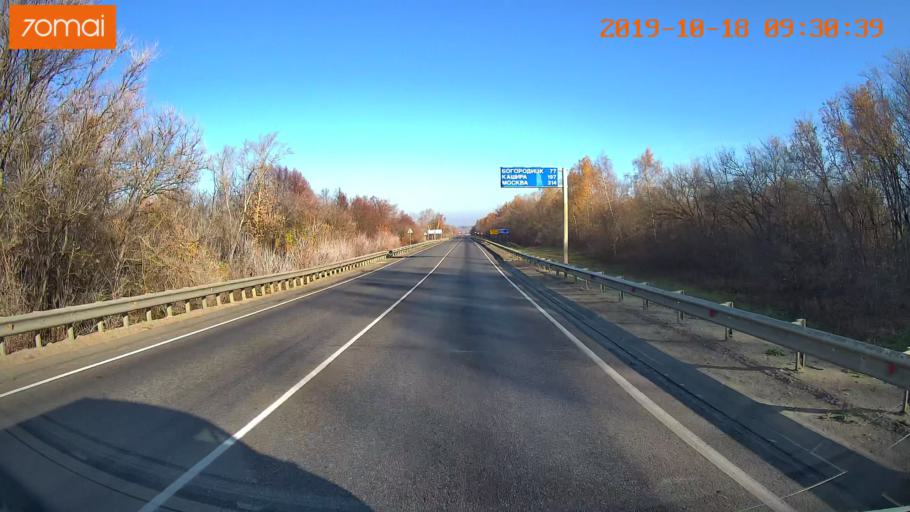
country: RU
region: Tula
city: Yefremov
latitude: 53.1407
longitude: 38.1595
